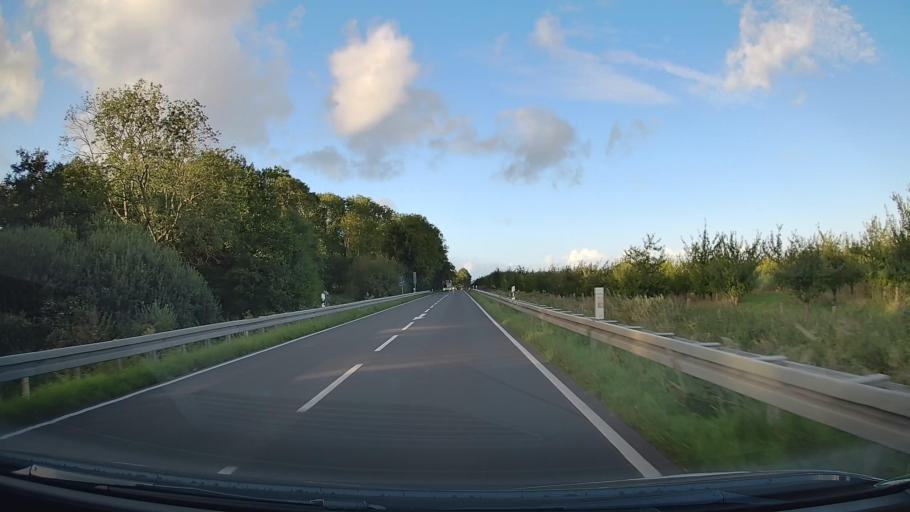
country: DE
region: Mecklenburg-Vorpommern
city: Wendorf
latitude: 54.2633
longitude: 13.0317
